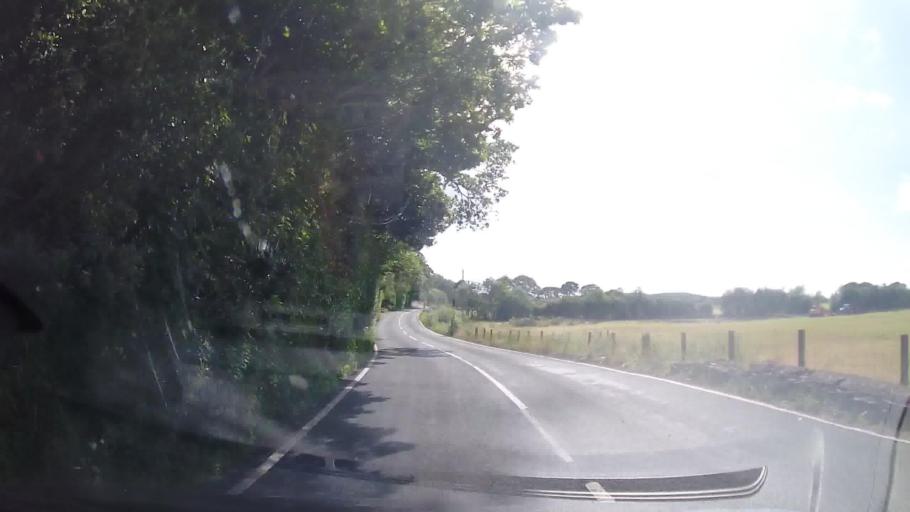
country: GB
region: Wales
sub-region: Gwynedd
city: Penrhyndeudraeth
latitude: 52.9093
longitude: -4.0544
